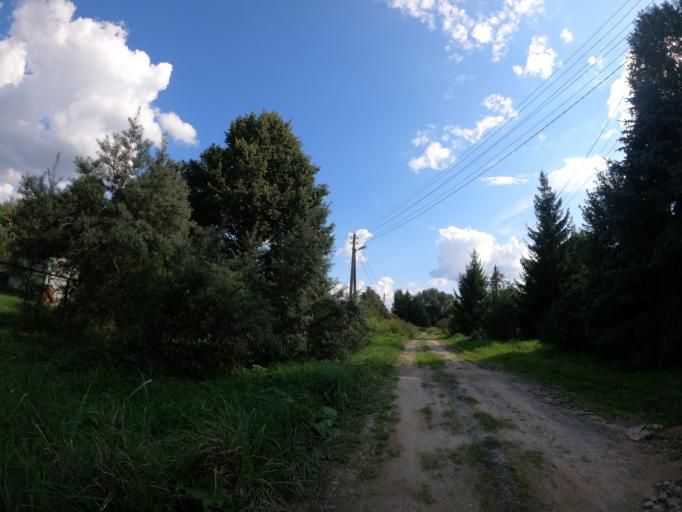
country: RU
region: Moskovskaya
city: Troitskoye
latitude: 55.2395
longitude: 38.4864
